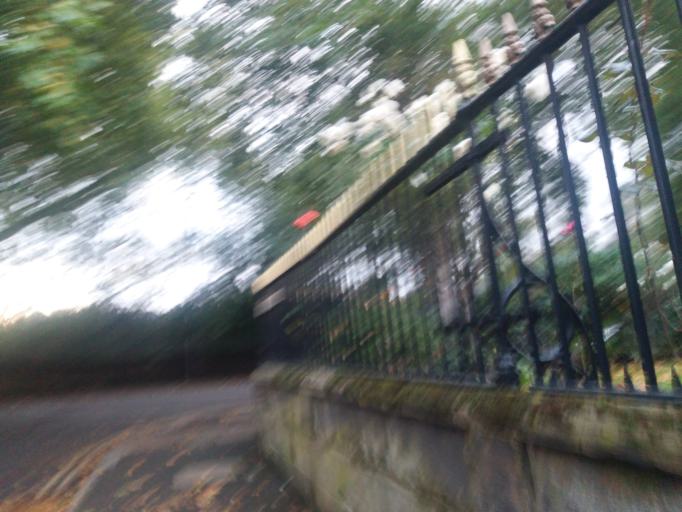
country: GB
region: England
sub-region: Derby
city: Derby
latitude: 52.9172
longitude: -1.4701
